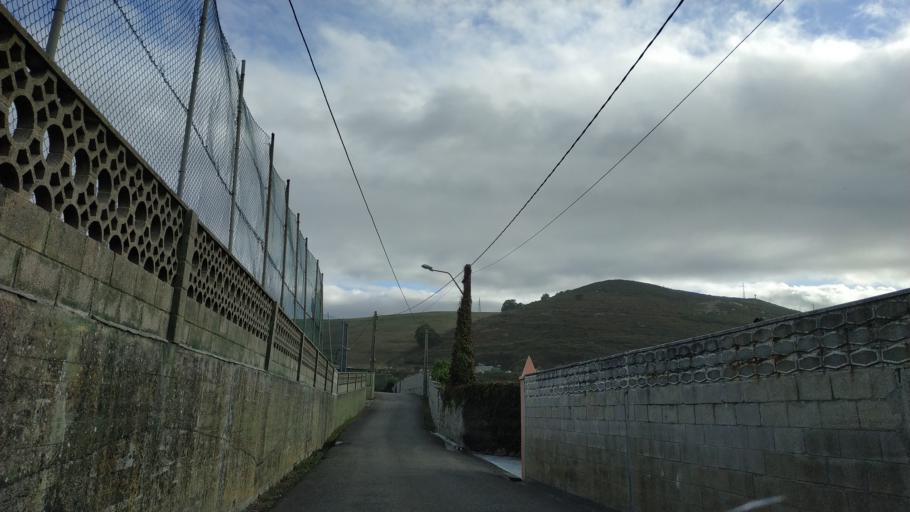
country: ES
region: Galicia
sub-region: Provincia da Coruna
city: A Coruna
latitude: 43.3752
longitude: -8.4463
